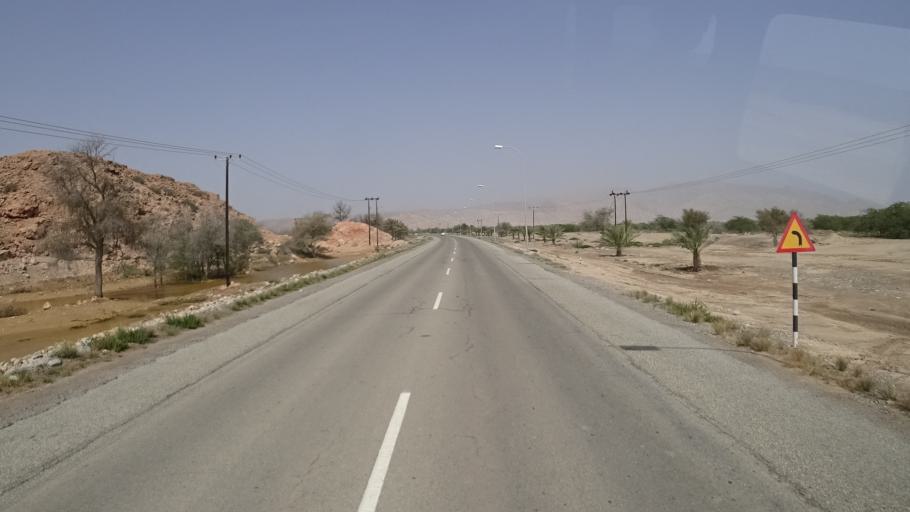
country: OM
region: Muhafazat Masqat
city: Muscat
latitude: 23.2140
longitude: 58.9355
